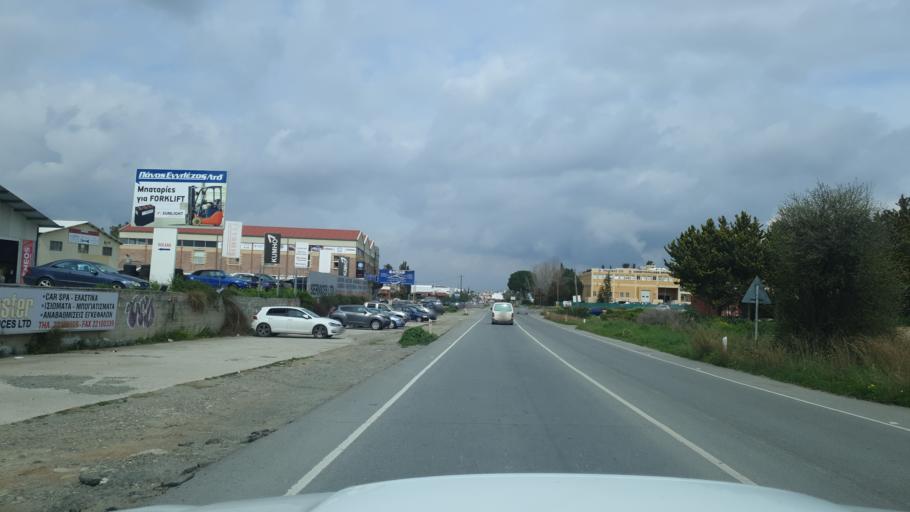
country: CY
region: Lefkosia
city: Geri
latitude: 35.0877
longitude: 33.3796
